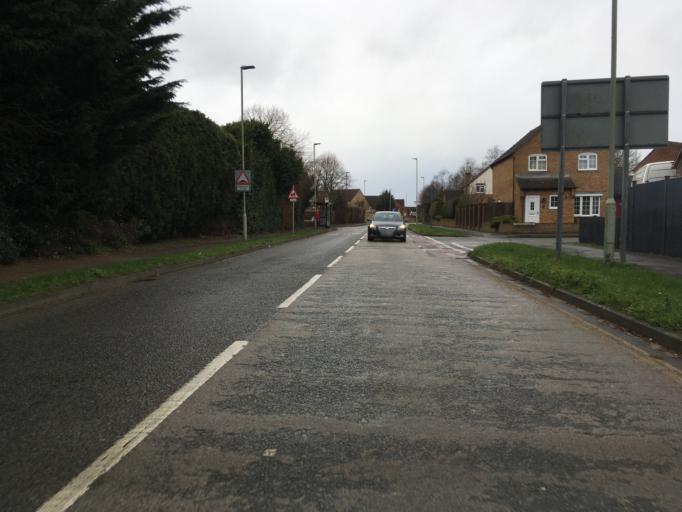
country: GB
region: England
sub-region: Gloucestershire
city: Gloucester
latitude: 51.8238
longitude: -2.2903
